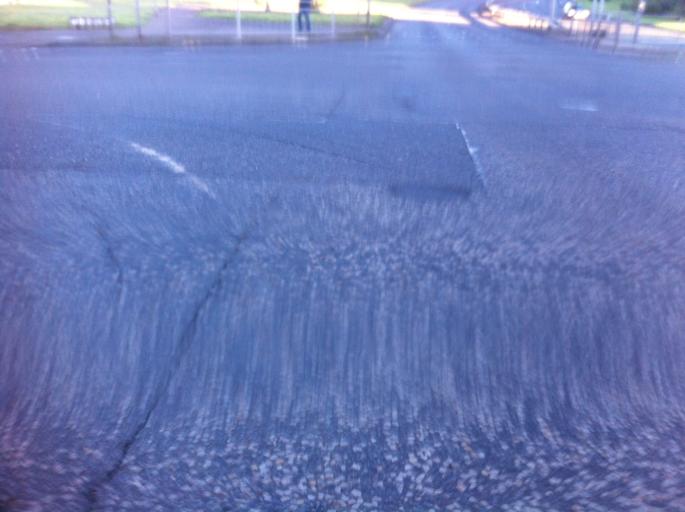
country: GB
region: Scotland
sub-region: Glasgow City
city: Glasgow
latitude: 55.8799
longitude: -4.2339
